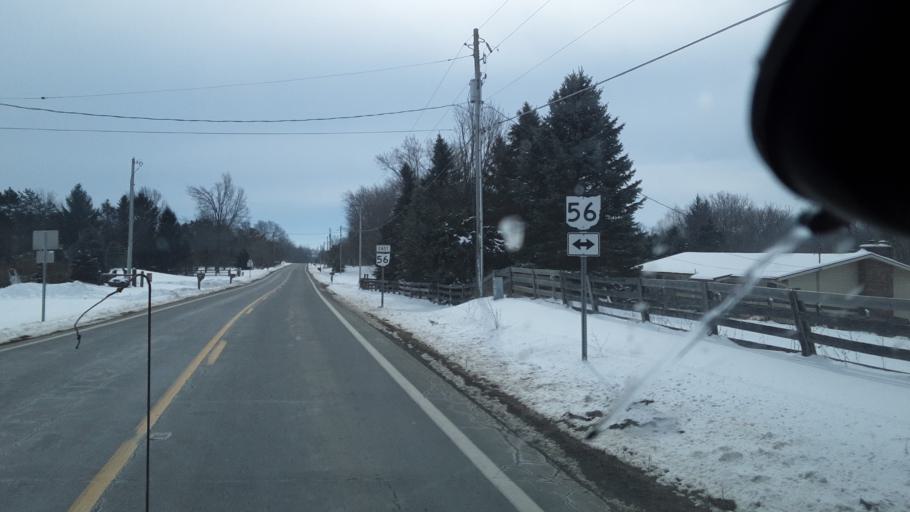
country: US
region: Ohio
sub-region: Madison County
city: Choctaw Lake
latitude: 39.9549
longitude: -83.5057
